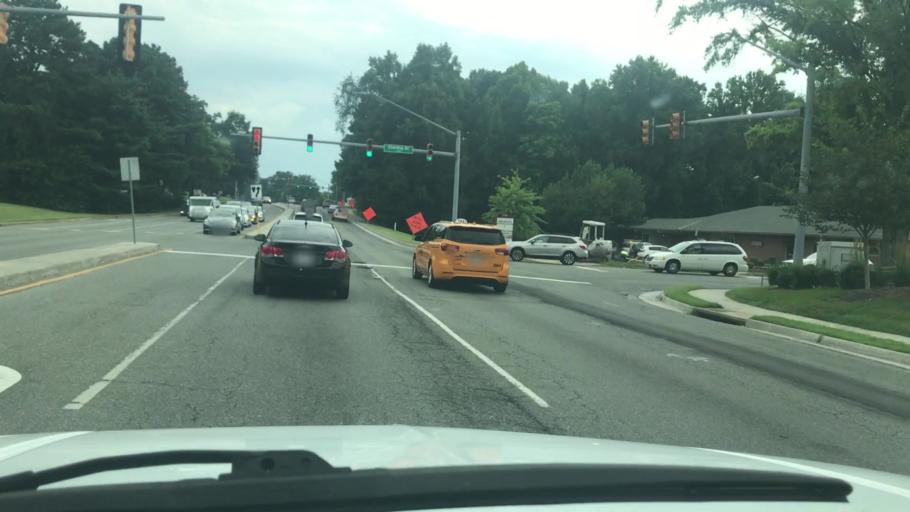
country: US
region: Virginia
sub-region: Henrico County
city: Tuckahoe
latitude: 37.6095
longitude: -77.5641
